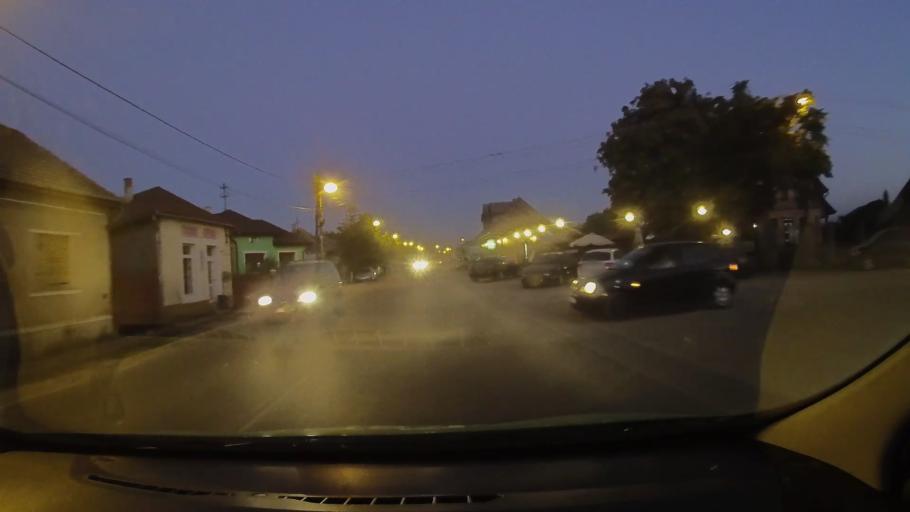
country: RO
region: Bihor
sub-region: Comuna Valea lui Mihai
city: Valea lui Mihai
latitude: 47.5145
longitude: 22.1376
